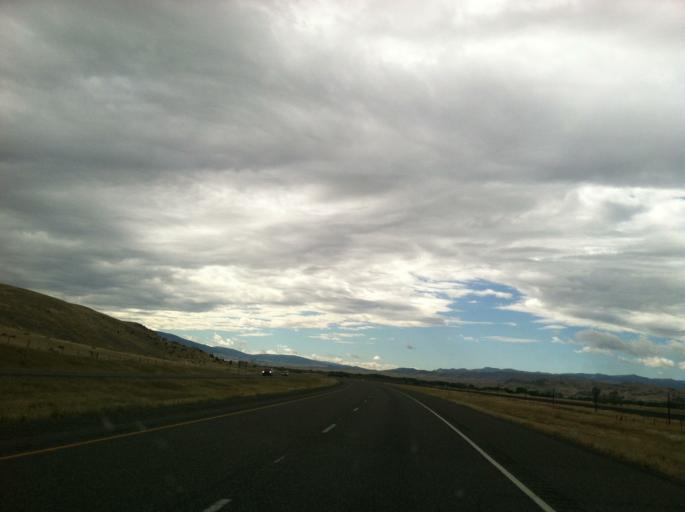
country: US
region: Montana
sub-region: Park County
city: Livingston
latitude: 45.7125
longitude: -110.4391
